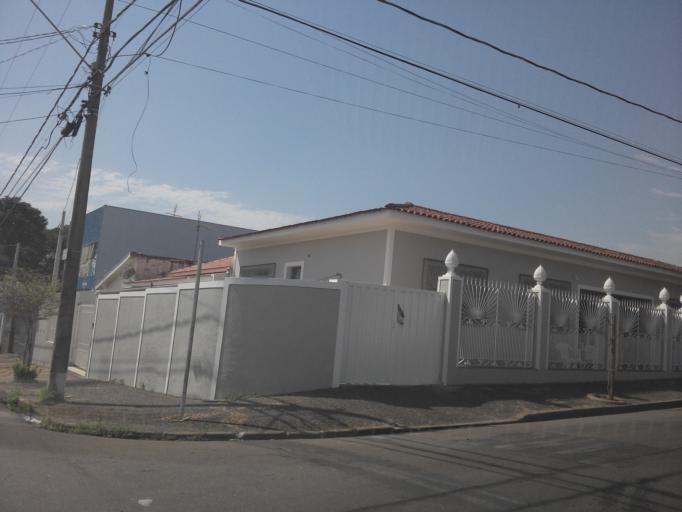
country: BR
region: Sao Paulo
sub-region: Sumare
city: Sumare
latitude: -22.8176
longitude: -47.2747
